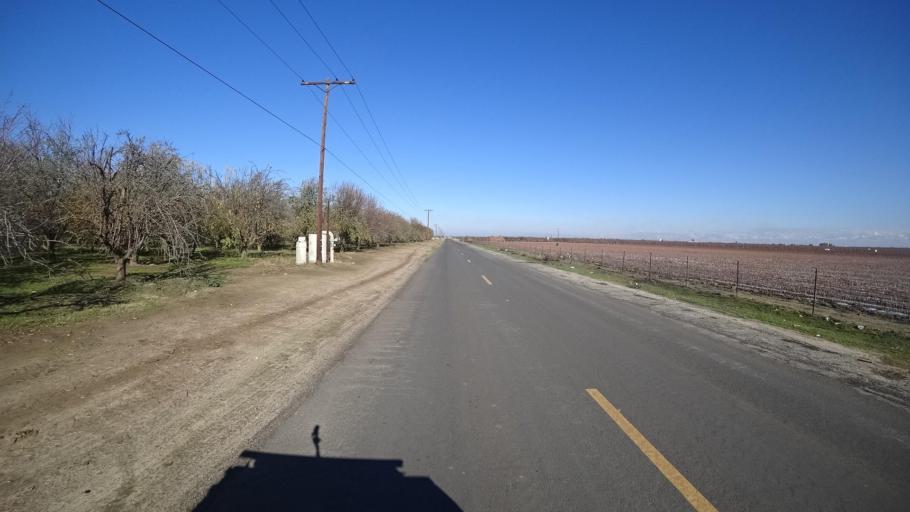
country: US
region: California
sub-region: Kern County
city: Delano
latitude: 35.7229
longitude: -119.2585
